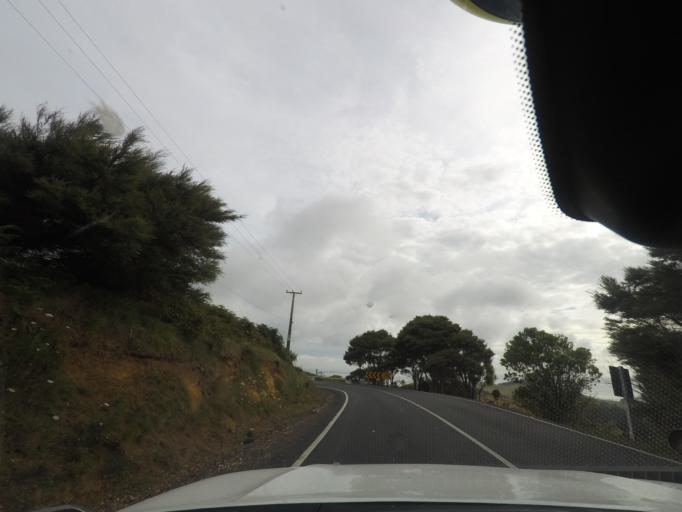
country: NZ
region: Auckland
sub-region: Auckland
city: Parakai
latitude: -36.4951
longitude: 174.2485
